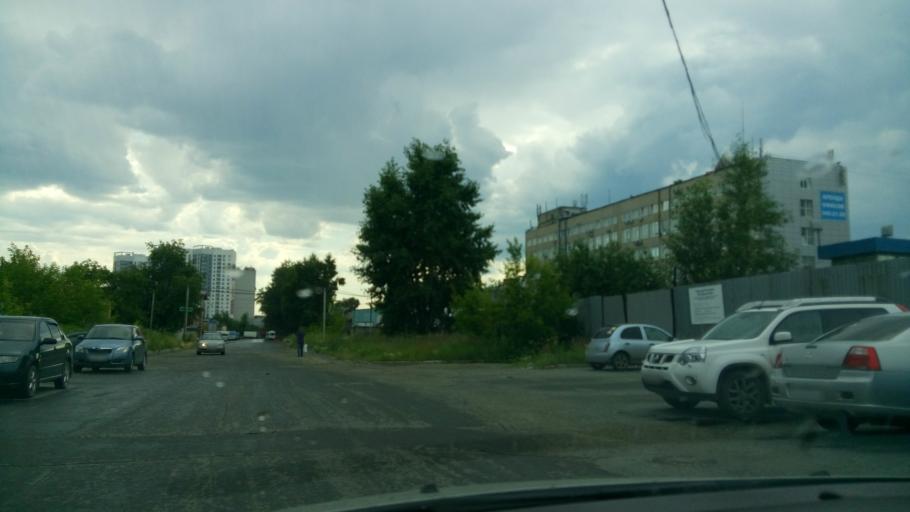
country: RU
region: Sverdlovsk
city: Yekaterinburg
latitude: 56.8630
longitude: 60.6691
